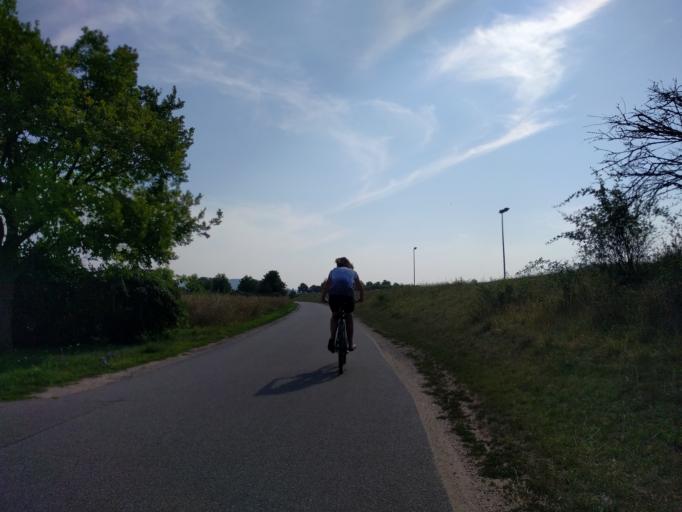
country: DE
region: Bavaria
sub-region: Upper Palatinate
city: Tegernheim
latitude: 49.0183
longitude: 12.1706
